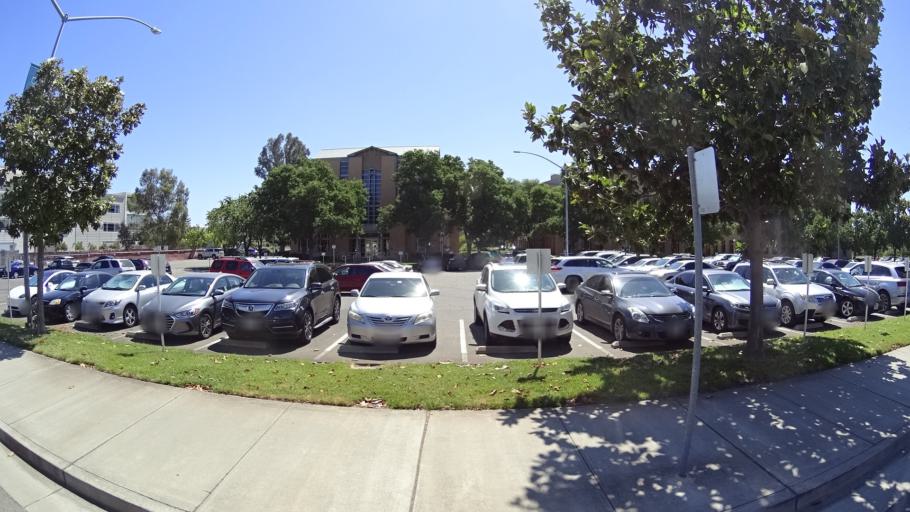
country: US
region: California
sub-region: Sacramento County
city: Sacramento
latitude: 38.5518
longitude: -121.4534
